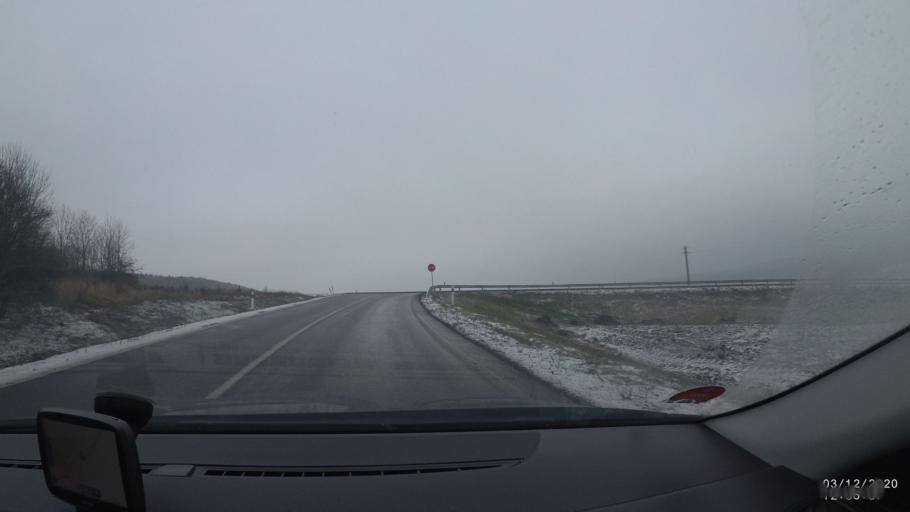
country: CZ
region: Central Bohemia
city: Revnicov
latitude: 50.1895
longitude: 13.8194
